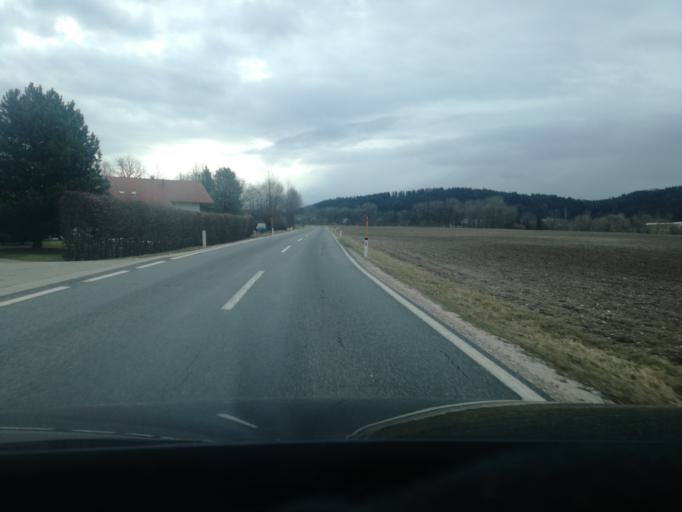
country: AT
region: Upper Austria
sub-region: Politischer Bezirk Vocklabruck
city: Neukirchen an der Vockla
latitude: 48.0256
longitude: 13.5163
